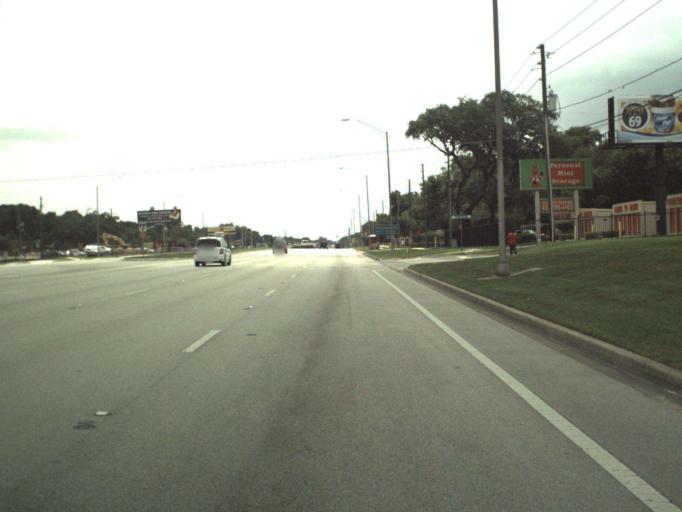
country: US
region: Florida
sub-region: Orange County
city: South Apopka
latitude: 28.6732
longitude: -81.4840
